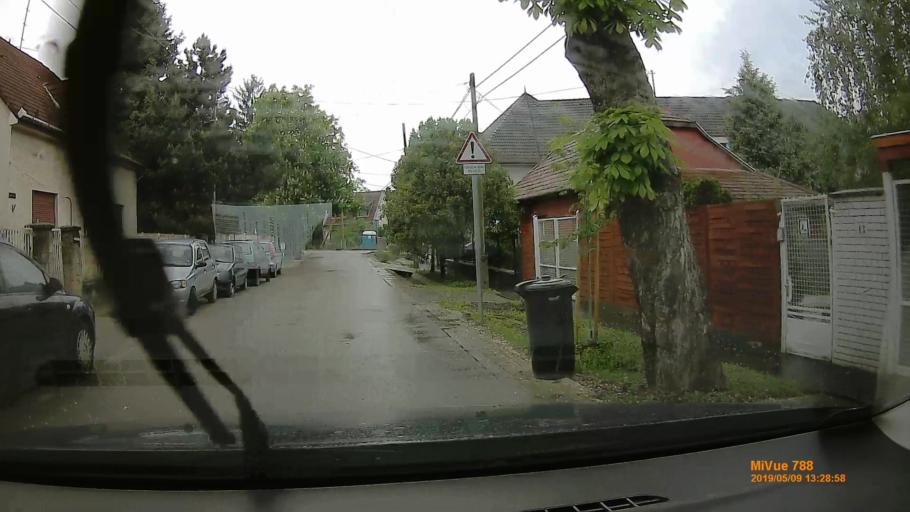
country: HU
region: Budapest
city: Budapest XVI. keruelet
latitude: 47.5360
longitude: 19.1964
